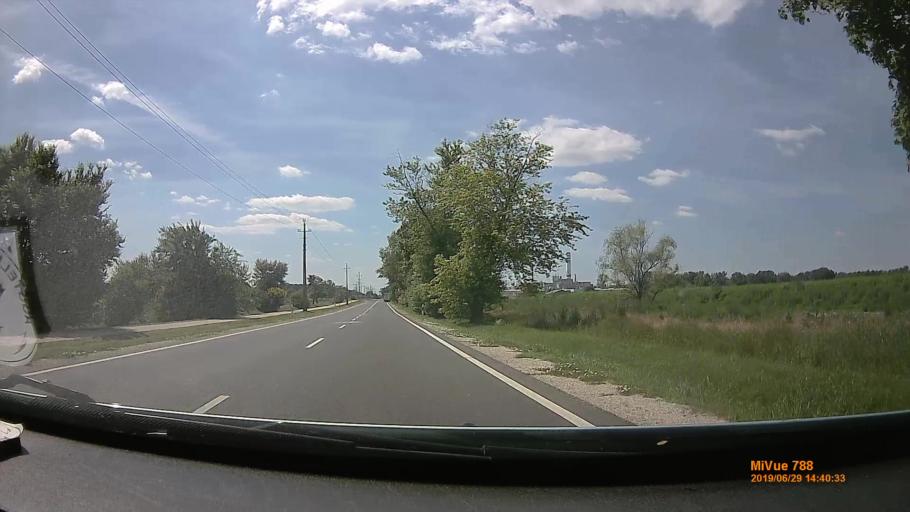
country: HU
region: Komarom-Esztergom
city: Nyergesujfalu
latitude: 47.7564
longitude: 18.5845
